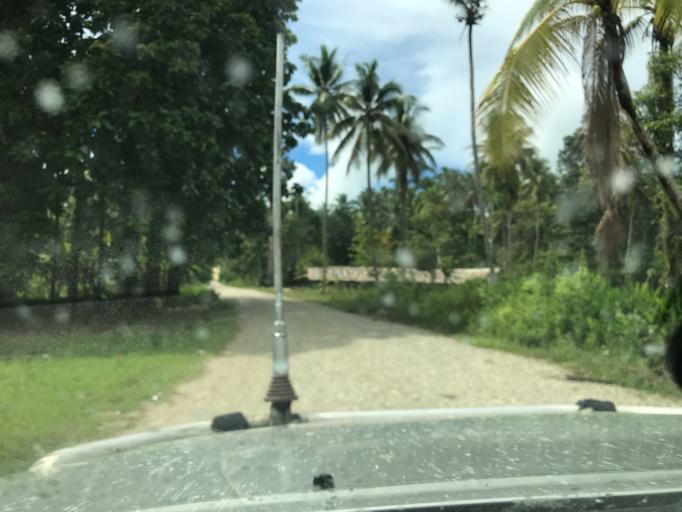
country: SB
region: Malaita
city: Auki
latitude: -8.3830
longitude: 160.6955
